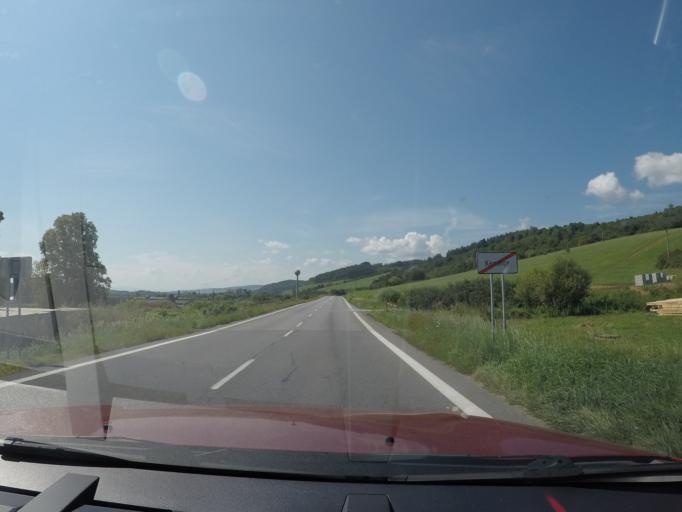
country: SK
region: Presovsky
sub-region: Okres Presov
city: Presov
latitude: 48.9204
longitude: 21.2409
